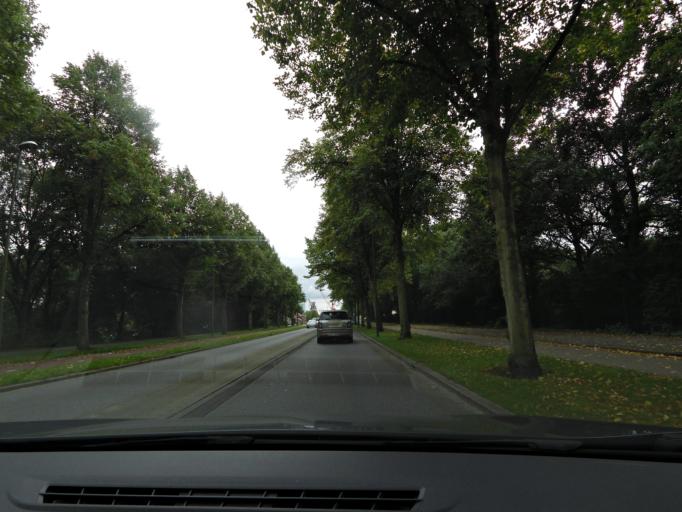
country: NL
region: South Holland
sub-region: Gemeente Schiedam
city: Schiedam
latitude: 51.9151
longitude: 4.3787
